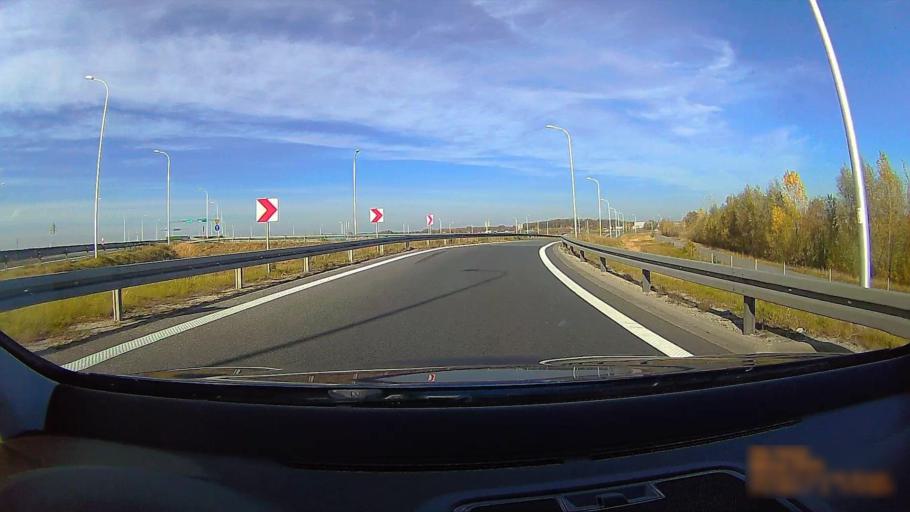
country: PL
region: Greater Poland Voivodeship
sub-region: Powiat ostrowski
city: Ostrow Wielkopolski
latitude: 51.6632
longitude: 17.8583
